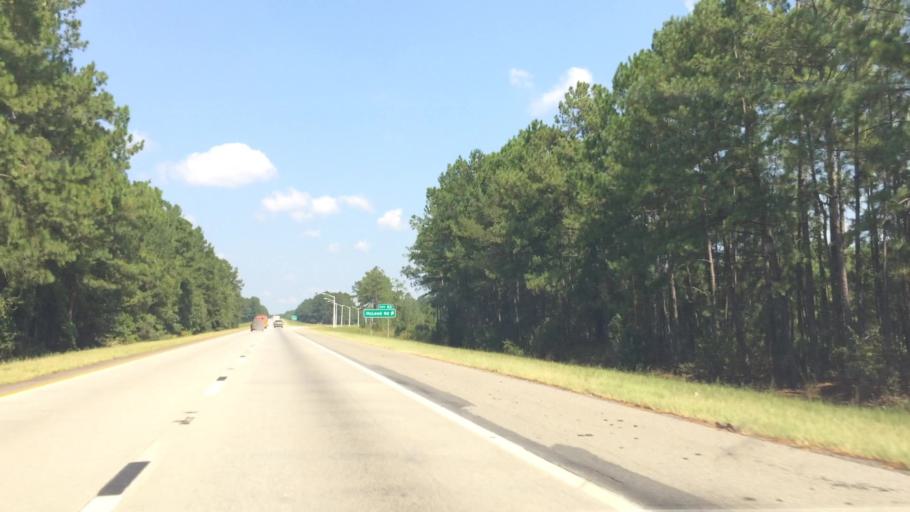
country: US
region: South Carolina
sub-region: Colleton County
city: Walterboro
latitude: 32.9957
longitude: -80.6705
